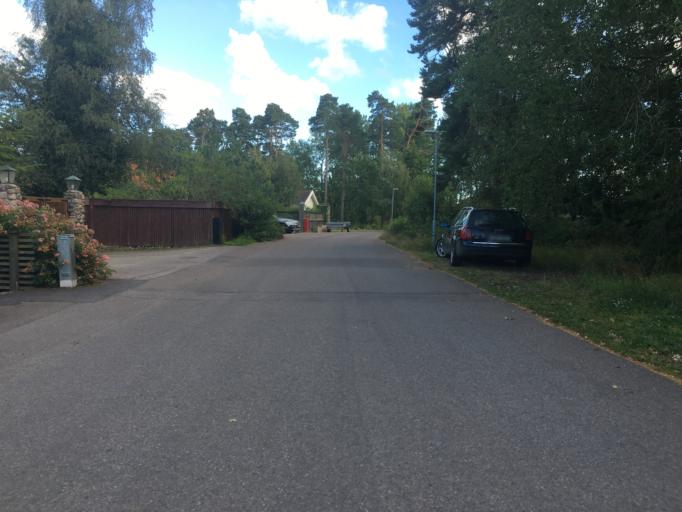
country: SE
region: Kalmar
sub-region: Kalmar Kommun
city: Kalmar
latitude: 56.7026
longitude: 16.3724
